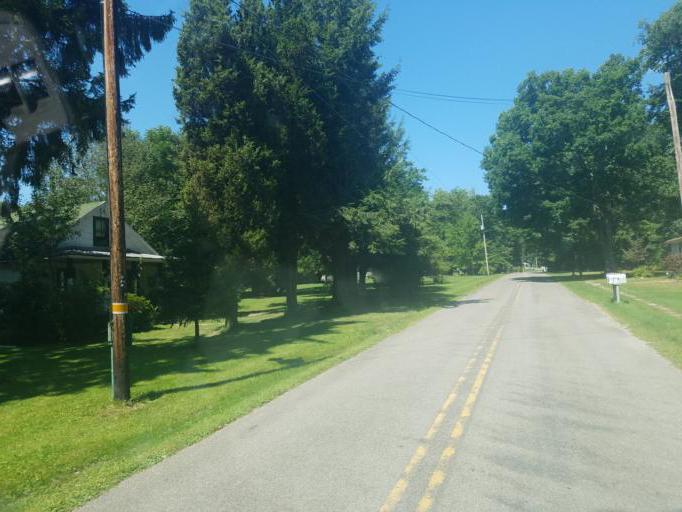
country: US
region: Pennsylvania
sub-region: Clarion County
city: Knox
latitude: 41.1917
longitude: -79.4902
